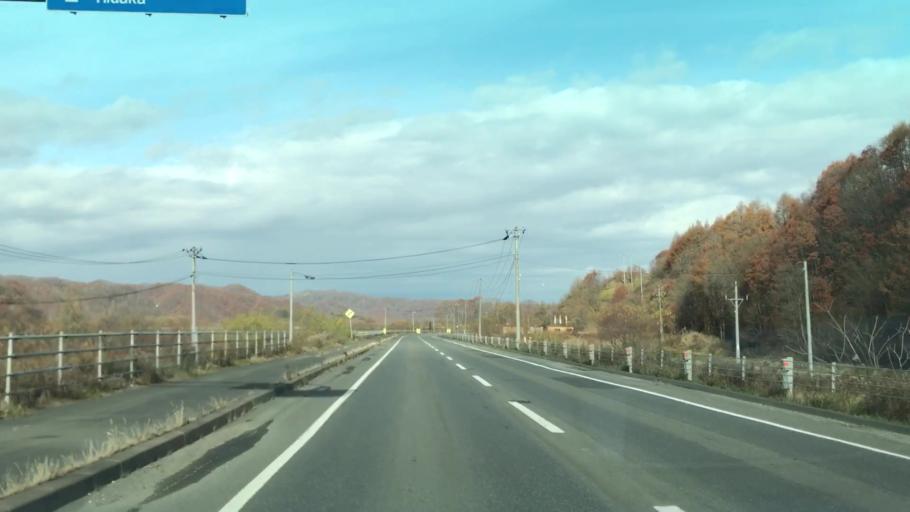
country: JP
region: Hokkaido
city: Shizunai-furukawacho
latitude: 42.5915
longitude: 142.1455
